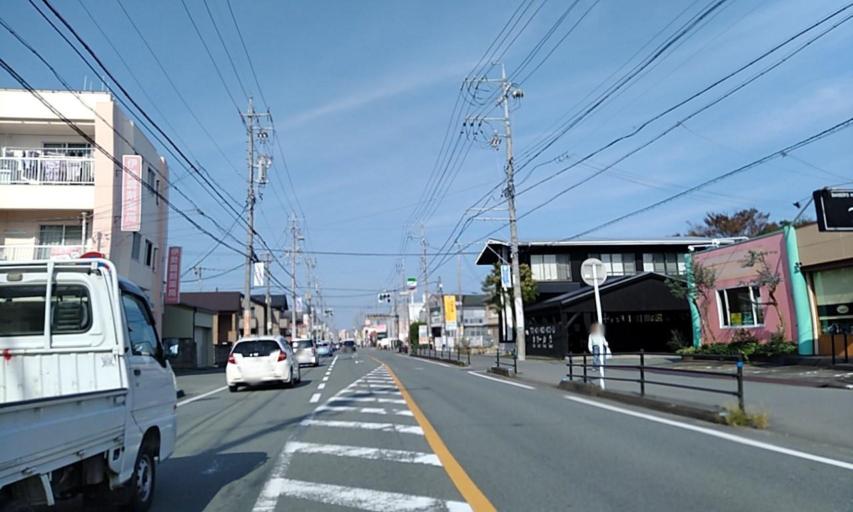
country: JP
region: Mie
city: Ise
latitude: 34.4975
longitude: 136.7150
